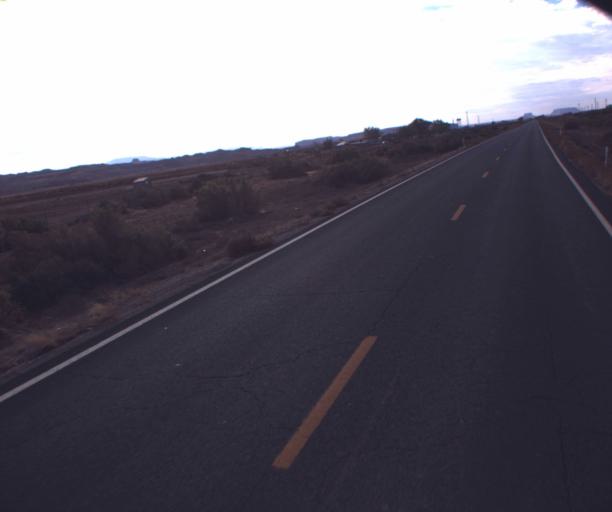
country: US
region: Arizona
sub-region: Apache County
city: Many Farms
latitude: 36.7351
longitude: -109.6337
